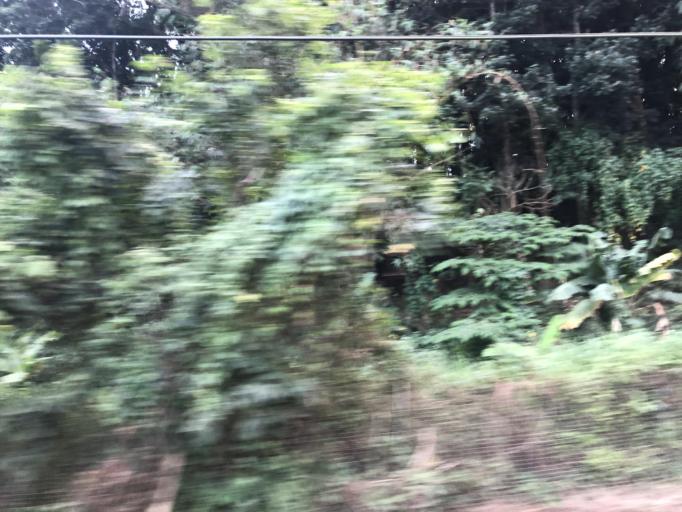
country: TW
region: Taiwan
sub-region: Tainan
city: Tainan
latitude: 23.0242
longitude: 120.3507
